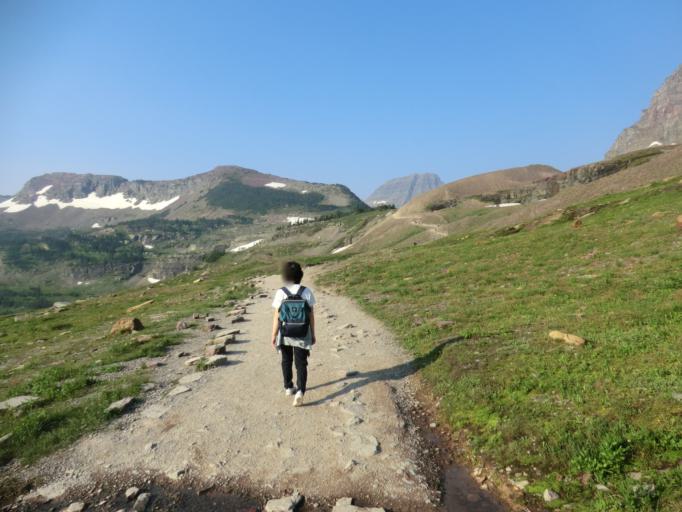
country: US
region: Montana
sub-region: Flathead County
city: Columbia Falls
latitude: 48.6918
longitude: -113.7299
